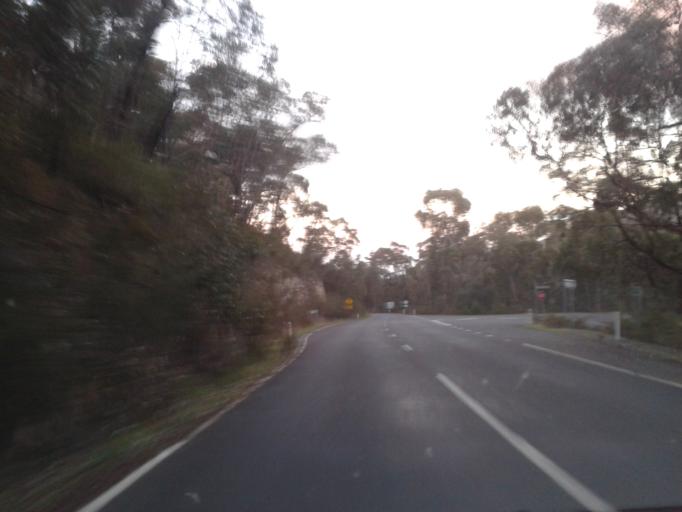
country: AU
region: Victoria
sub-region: Northern Grampians
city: Stawell
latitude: -37.1592
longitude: 142.4969
